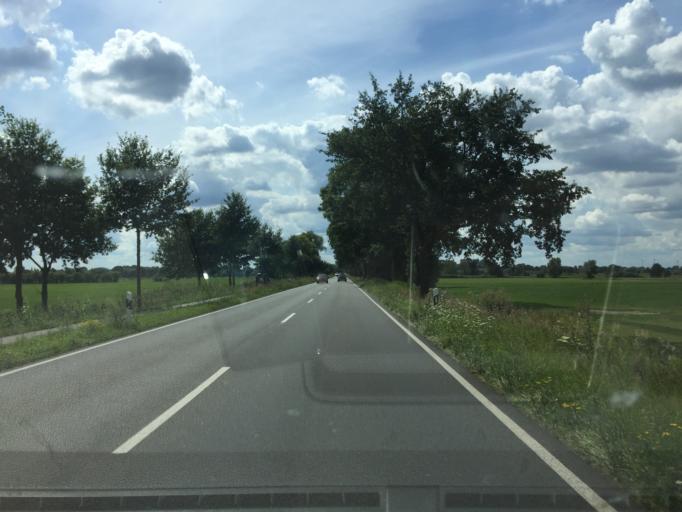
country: DE
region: Lower Saxony
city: Hauslingen
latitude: 52.7901
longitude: 9.3994
